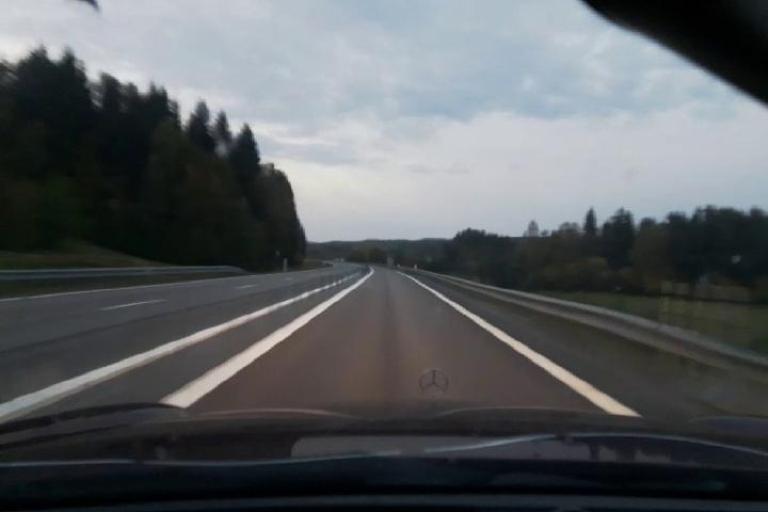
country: SE
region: Vaesternorrland
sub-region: Kramfors Kommun
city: Nordingra
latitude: 62.9721
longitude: 18.1607
